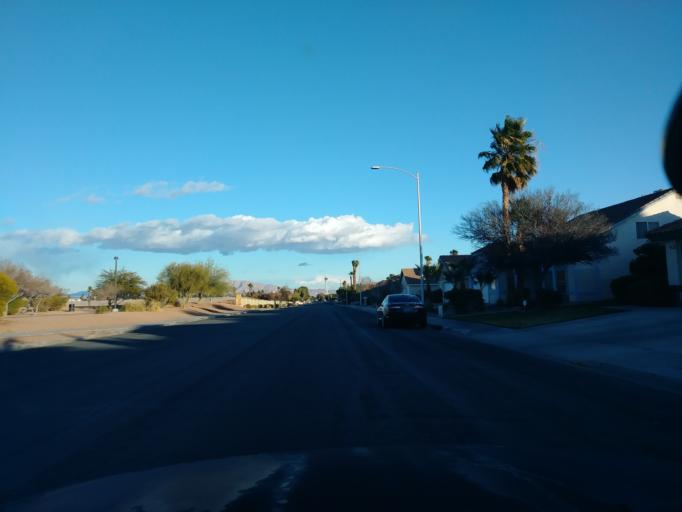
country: US
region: Nevada
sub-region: Clark County
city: Spring Valley
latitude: 36.1479
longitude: -115.2374
